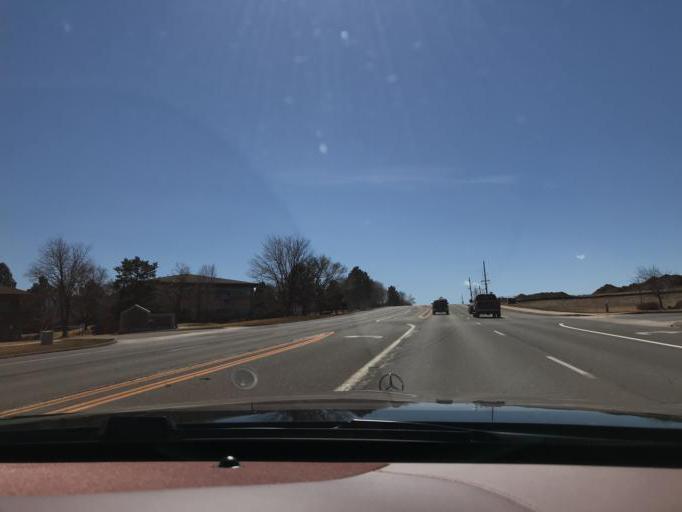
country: US
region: Colorado
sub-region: Jefferson County
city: Applewood
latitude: 39.7965
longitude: -105.1380
